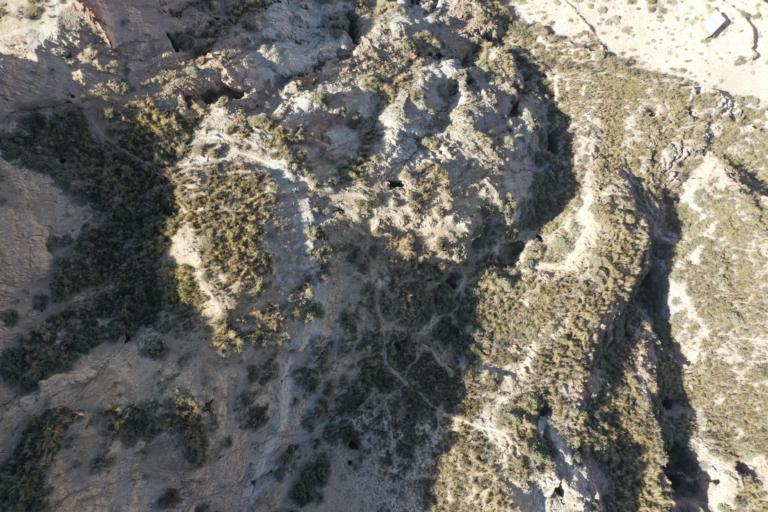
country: BO
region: La Paz
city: La Paz
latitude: -16.5521
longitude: -68.1292
